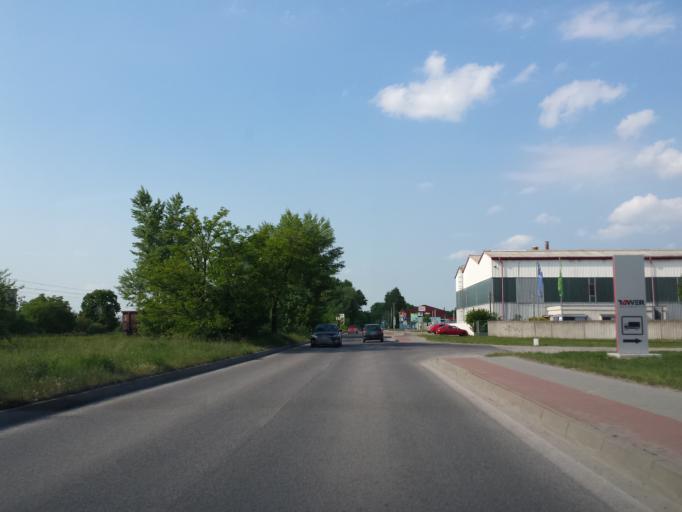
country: SK
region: Bratislavsky
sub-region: Okres Malacky
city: Malacky
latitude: 48.4208
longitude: 17.0216
